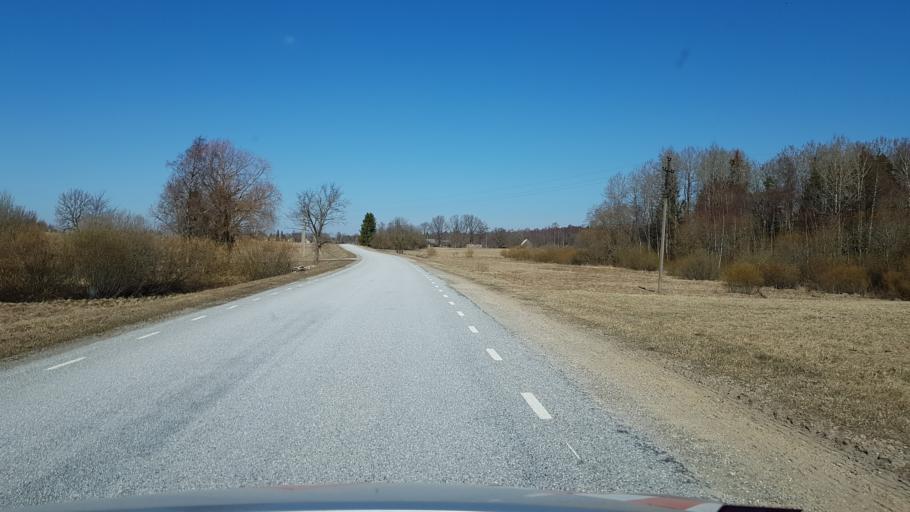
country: EE
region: Jaervamaa
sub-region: Koeru vald
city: Koeru
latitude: 59.0400
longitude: 26.0918
